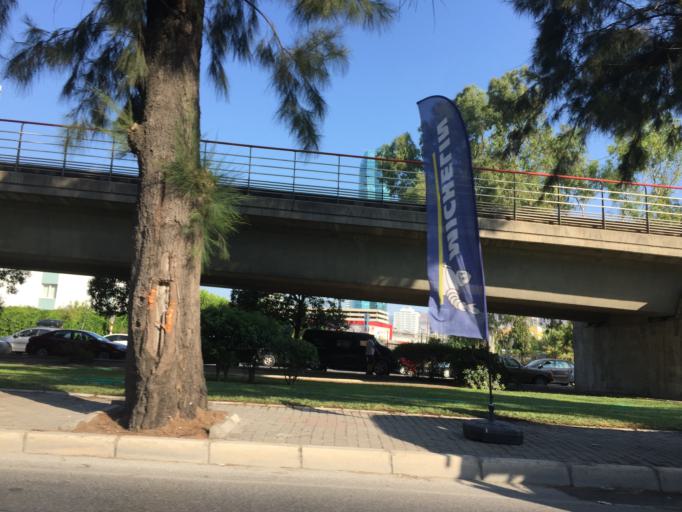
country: TR
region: Izmir
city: Buca
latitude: 38.4436
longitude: 27.1830
